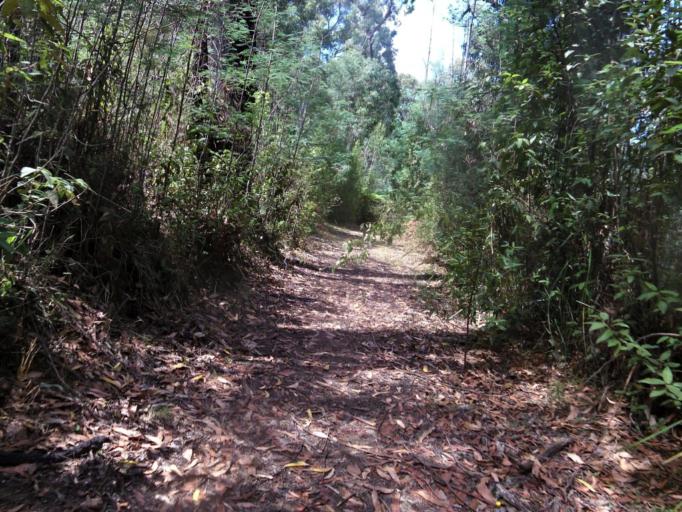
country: AU
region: Victoria
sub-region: Yarra Ranges
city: Healesville
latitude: -37.4221
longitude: 145.5677
